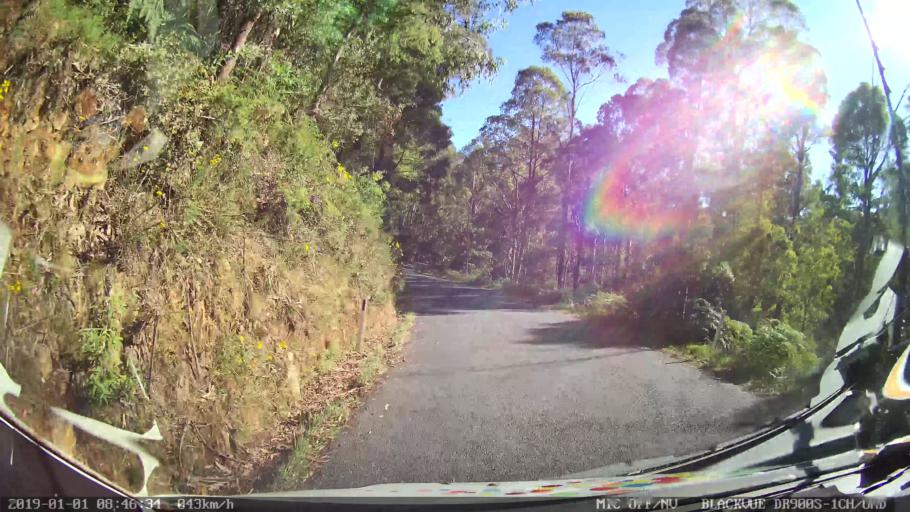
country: AU
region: New South Wales
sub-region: Snowy River
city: Jindabyne
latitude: -36.2994
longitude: 148.1940
